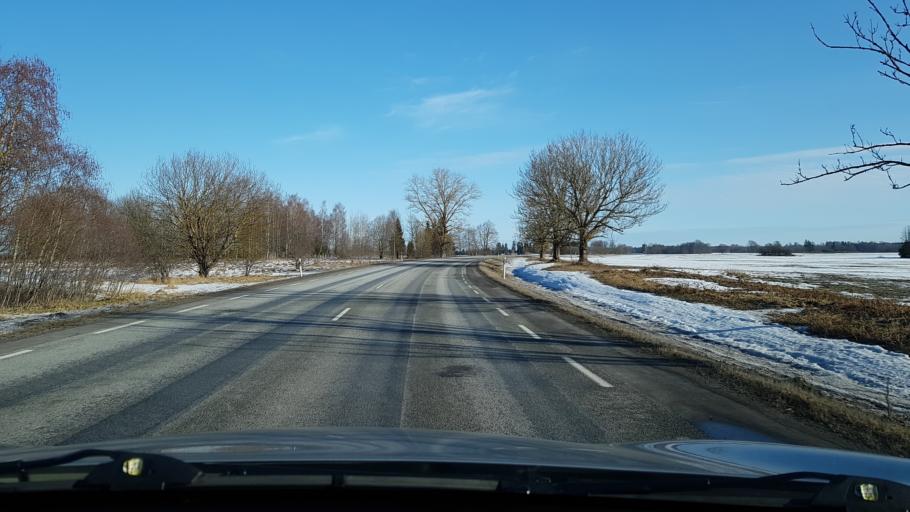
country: EE
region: Viljandimaa
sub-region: Vohma linn
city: Vohma
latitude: 58.6518
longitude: 25.5902
